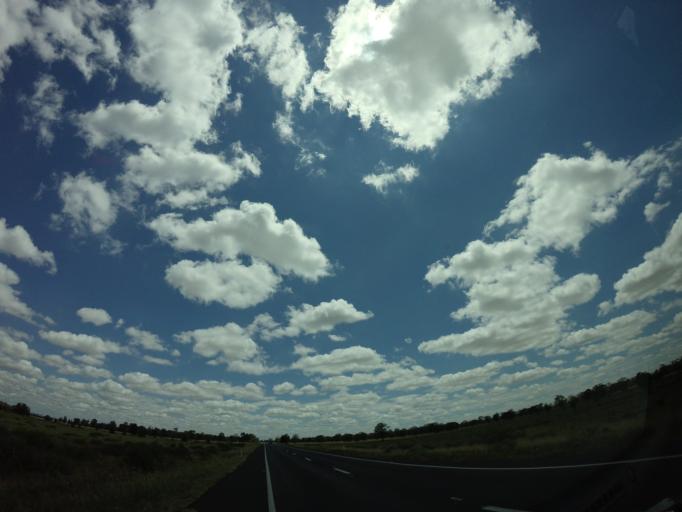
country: AU
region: New South Wales
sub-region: Moree Plains
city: Moree
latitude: -29.0949
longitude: 150.0354
